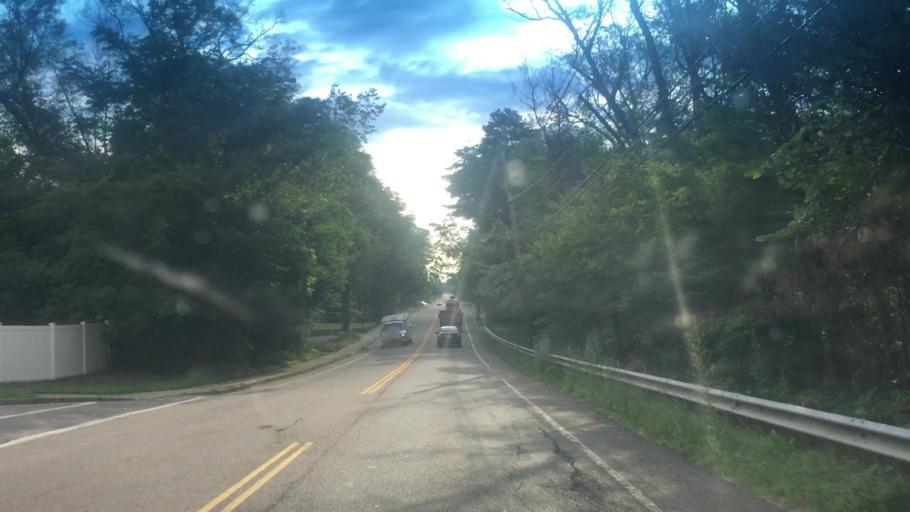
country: US
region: Massachusetts
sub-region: Norfolk County
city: Medway
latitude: 42.1551
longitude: -71.3975
